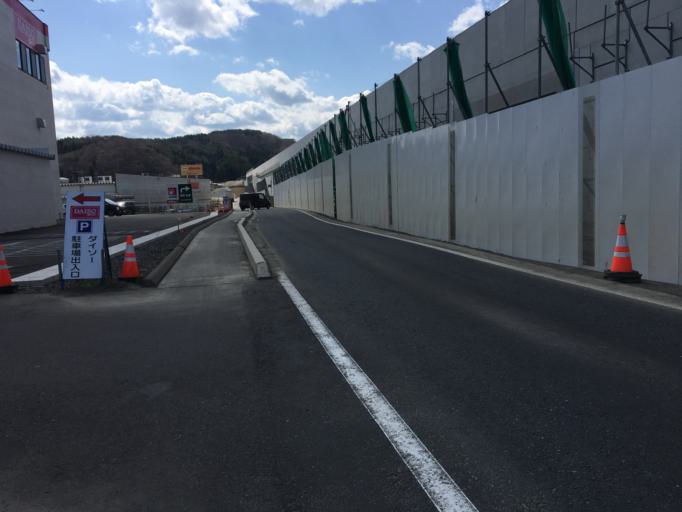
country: JP
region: Aomori
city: Hachinohe
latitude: 40.1910
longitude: 141.7868
